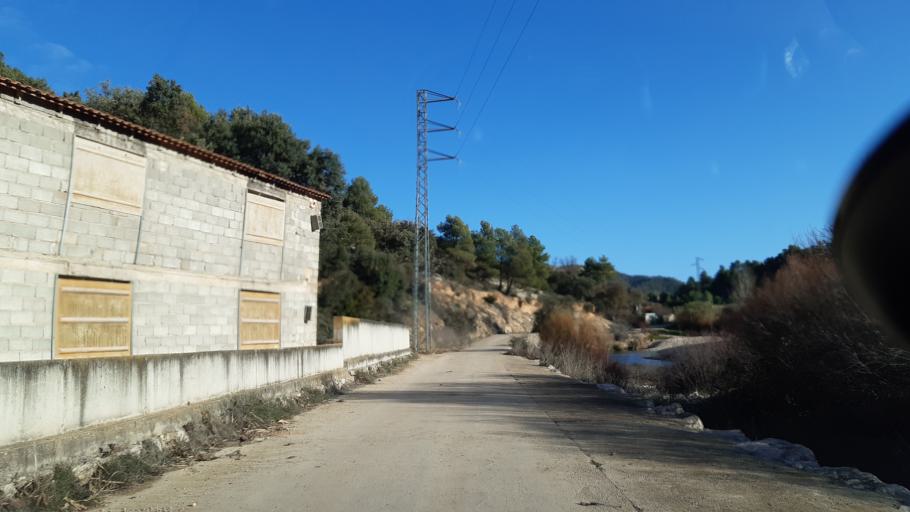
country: ES
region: Aragon
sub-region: Provincia de Teruel
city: Valderrobres
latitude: 40.8442
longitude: 0.2047
